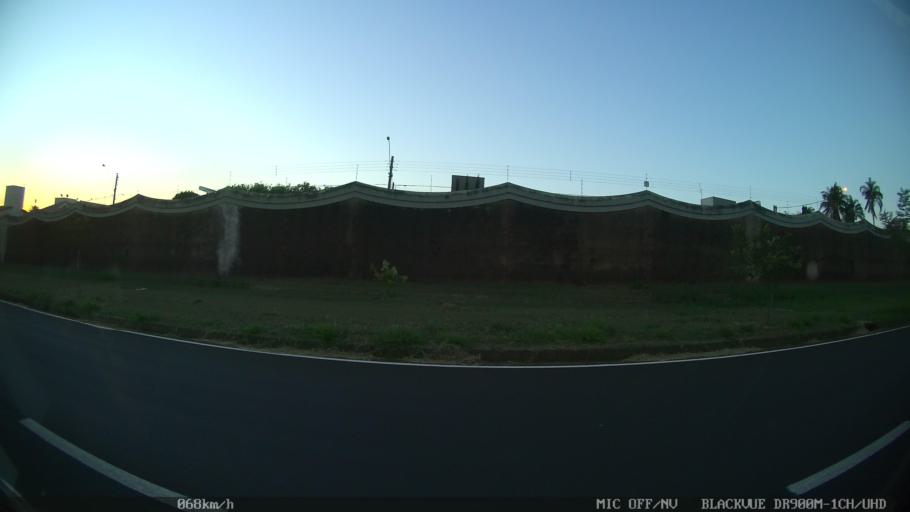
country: BR
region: Sao Paulo
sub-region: Sao Jose Do Rio Preto
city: Sao Jose do Rio Preto
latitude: -20.8163
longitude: -49.3448
